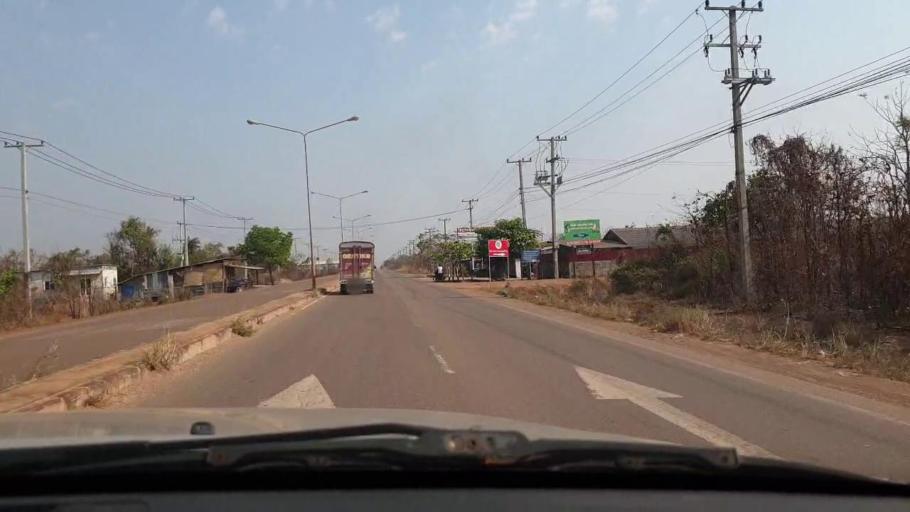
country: LA
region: Vientiane
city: Vientiane
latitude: 18.0159
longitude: 102.7241
